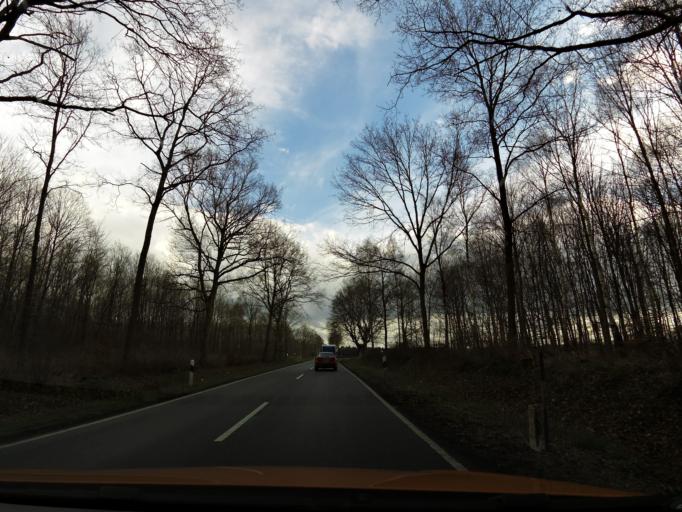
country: DE
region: Lower Saxony
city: Harpstedt
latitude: 52.9070
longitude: 8.6053
